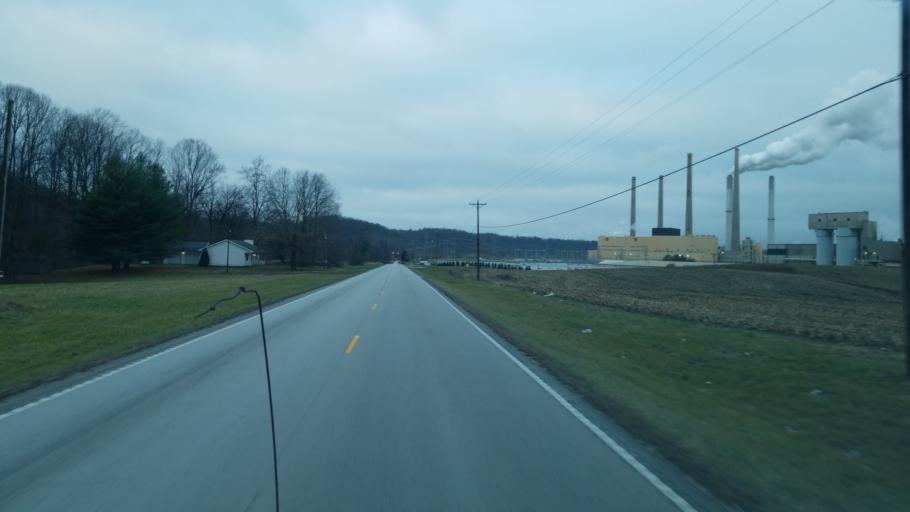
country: US
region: Ohio
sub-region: Brown County
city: Aberdeen
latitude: 38.6903
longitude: -83.8034
